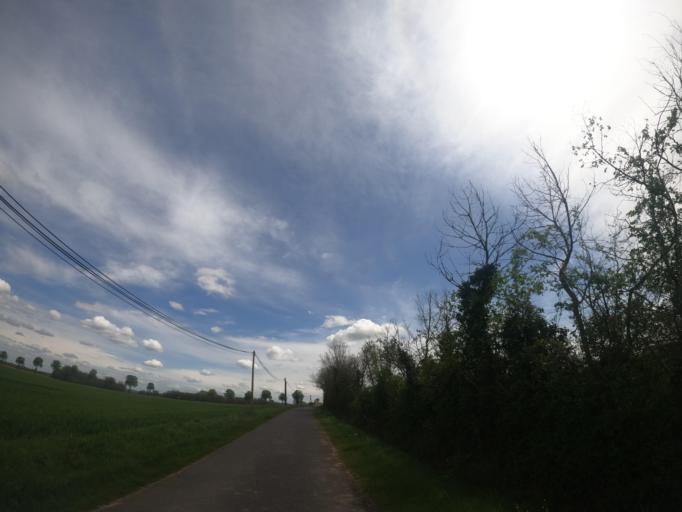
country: FR
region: Poitou-Charentes
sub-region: Departement des Deux-Sevres
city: Saint-Jean-de-Thouars
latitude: 46.9259
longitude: -0.2014
